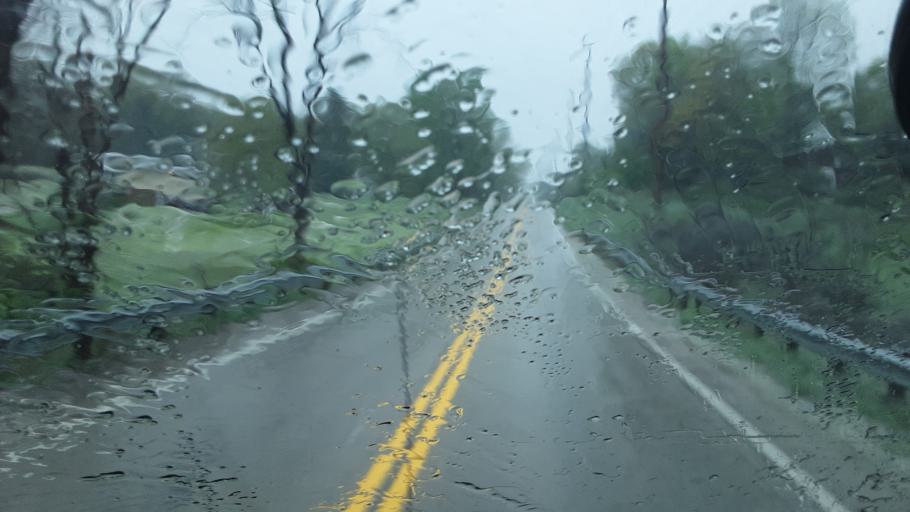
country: US
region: Ohio
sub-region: Portage County
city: Windham
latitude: 41.3087
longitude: -80.9896
